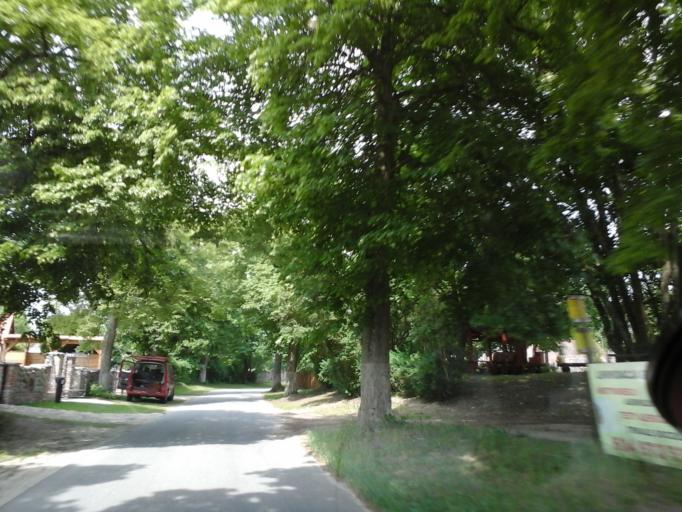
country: PL
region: West Pomeranian Voivodeship
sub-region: Powiat choszczenski
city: Drawno
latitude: 53.1316
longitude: 15.8463
